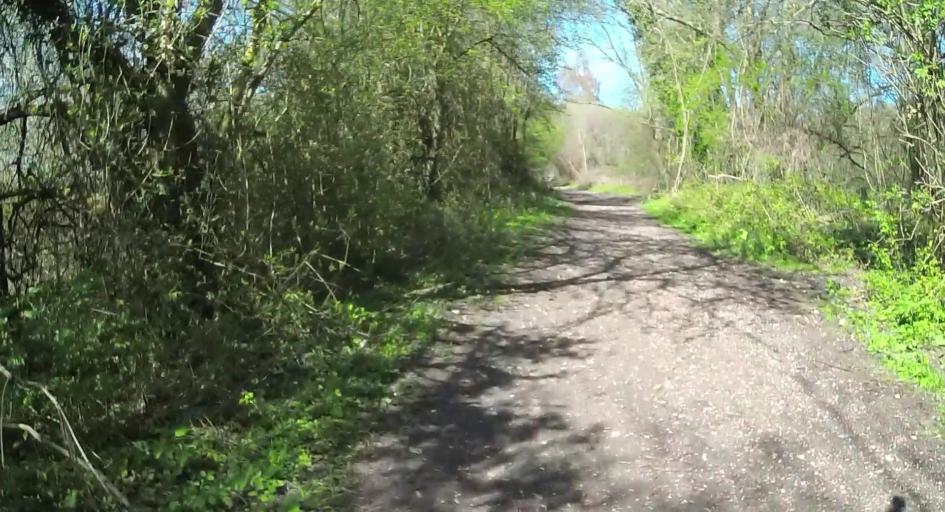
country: GB
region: England
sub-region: Hampshire
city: Abbotts Ann
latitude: 51.1057
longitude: -1.4937
